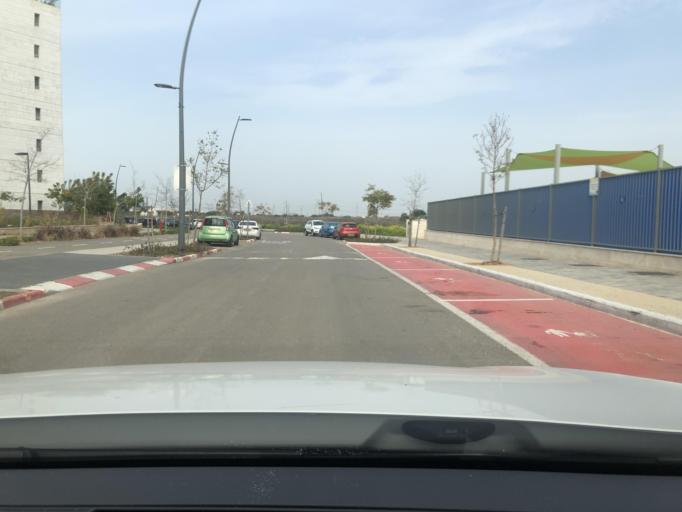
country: IL
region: Central District
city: Rosh Ha'Ayin
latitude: 32.1061
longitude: 34.9489
